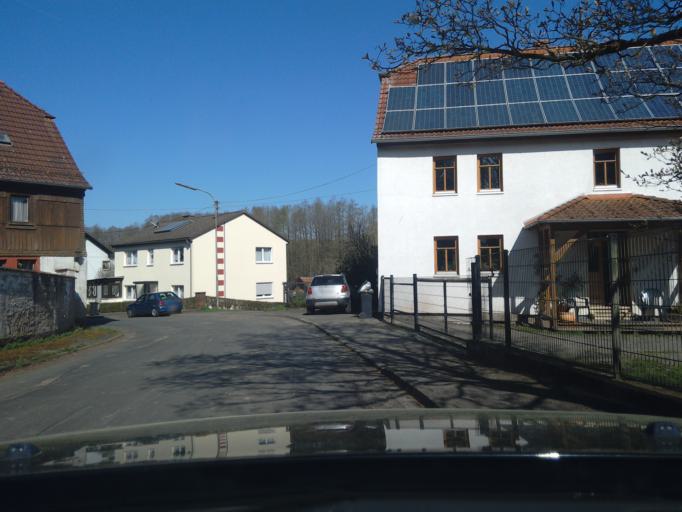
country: DE
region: Hesse
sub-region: Regierungsbezirk Darmstadt
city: Birstein
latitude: 50.3437
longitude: 9.3631
